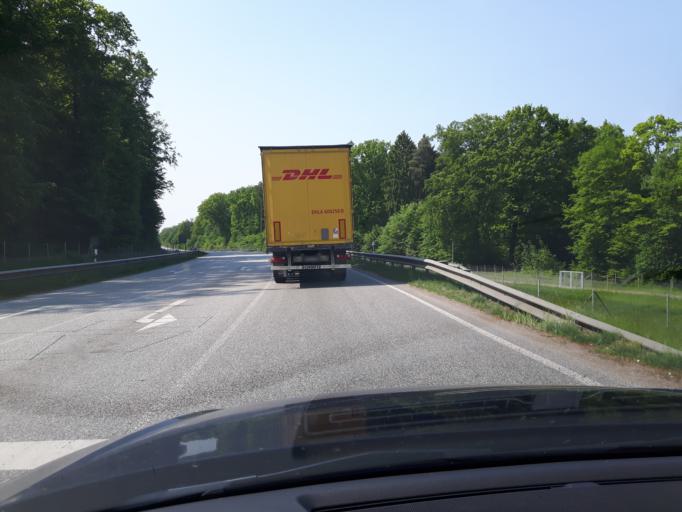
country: DE
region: Schleswig-Holstein
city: Ratekau
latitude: 53.8897
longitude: 10.7688
